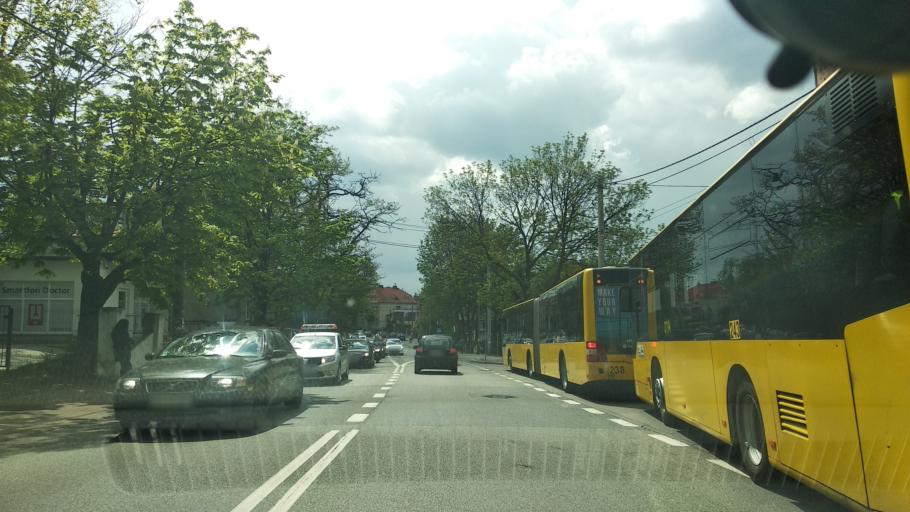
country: PL
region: Silesian Voivodeship
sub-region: Katowice
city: Katowice
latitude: 50.2299
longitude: 18.9712
